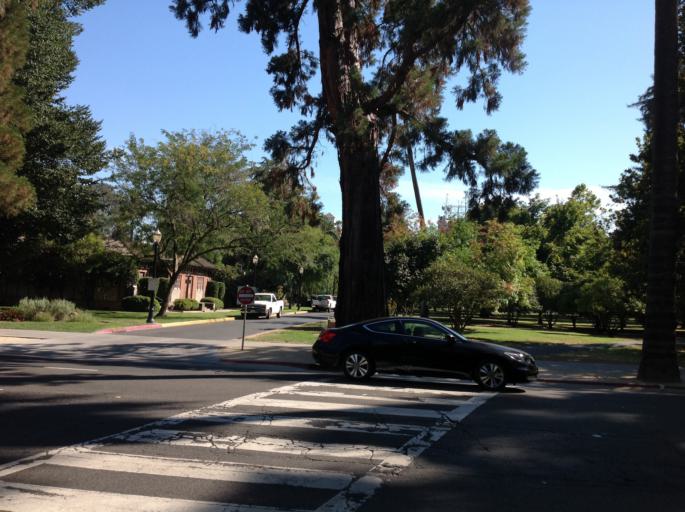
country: US
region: California
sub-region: Sacramento County
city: Sacramento
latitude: 38.5771
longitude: -121.4903
